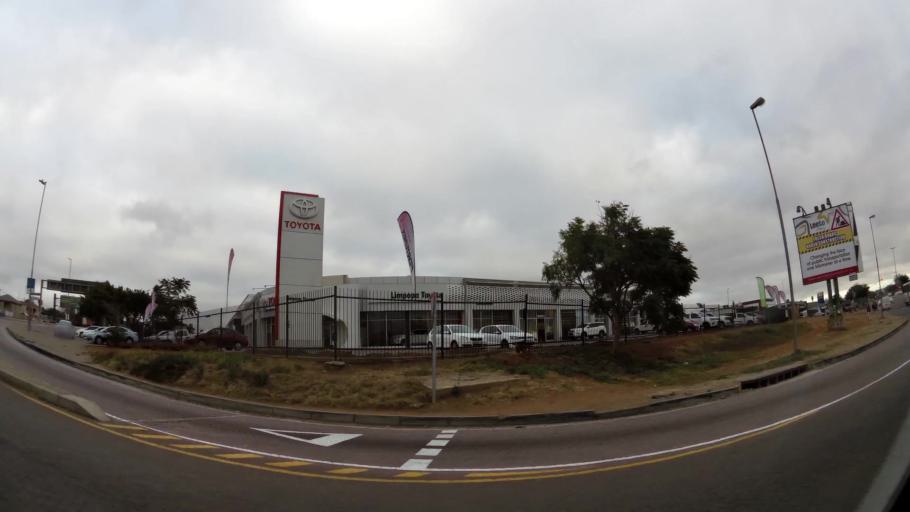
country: ZA
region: Limpopo
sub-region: Capricorn District Municipality
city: Polokwane
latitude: -23.9151
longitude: 29.4435
